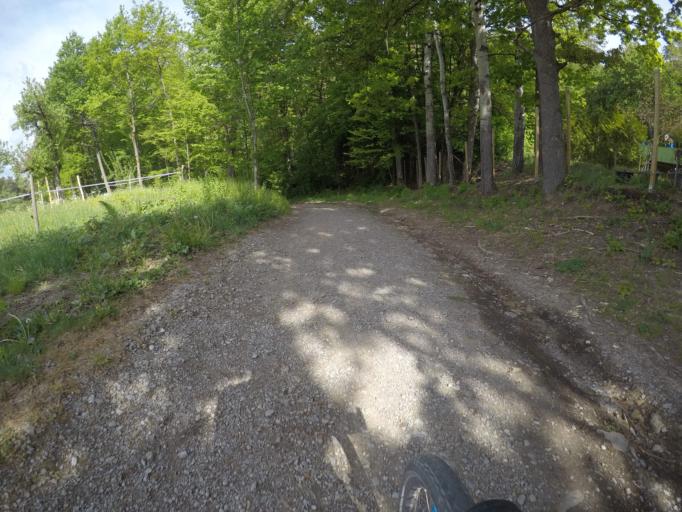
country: DE
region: Baden-Wuerttemberg
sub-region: Tuebingen Region
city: Tuebingen
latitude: 48.5403
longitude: 9.0250
